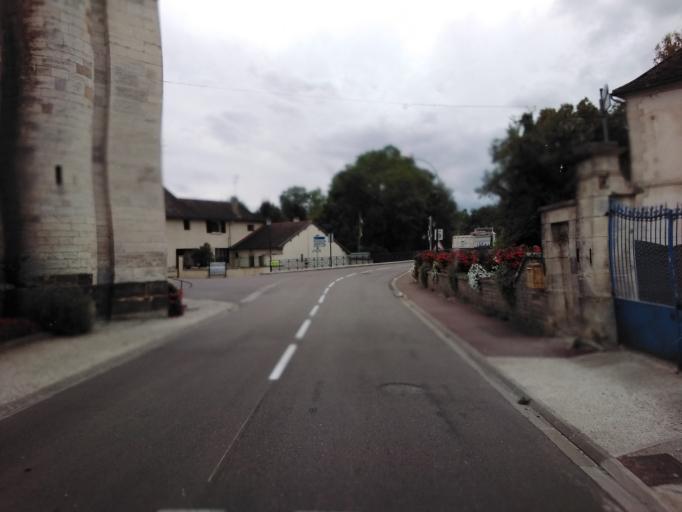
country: FR
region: Champagne-Ardenne
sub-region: Departement de l'Aube
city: Brienne-le-Chateau
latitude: 48.3493
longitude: 4.5318
